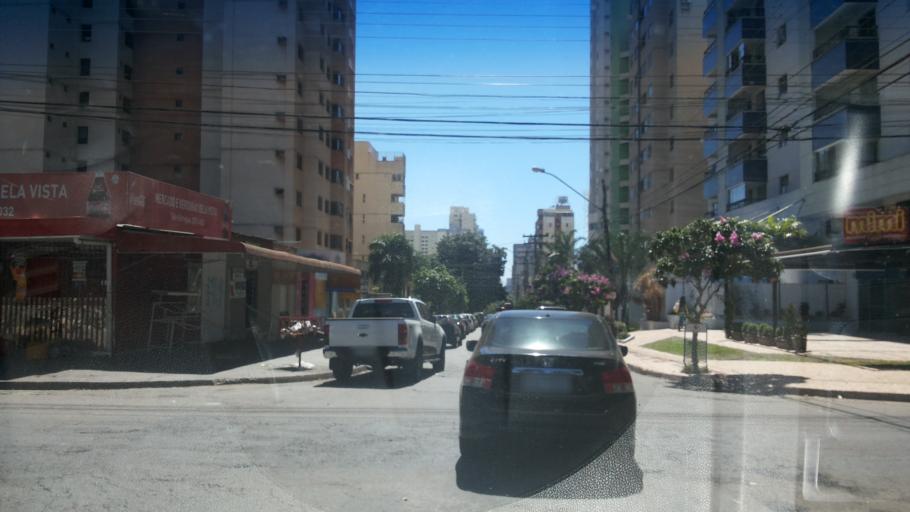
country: BR
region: Goias
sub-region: Goiania
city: Goiania
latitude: -16.7175
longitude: -49.2619
